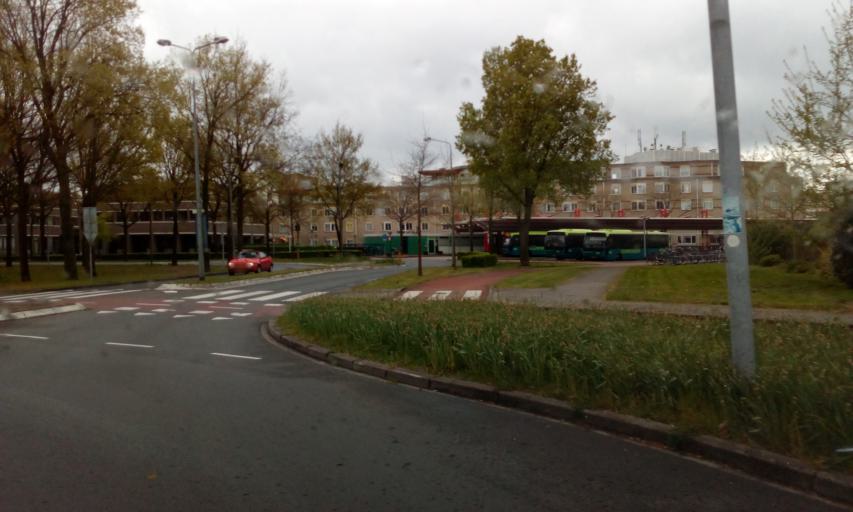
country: NL
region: North Holland
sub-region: Gemeente Huizen
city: Huizen
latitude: 52.2999
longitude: 5.2440
